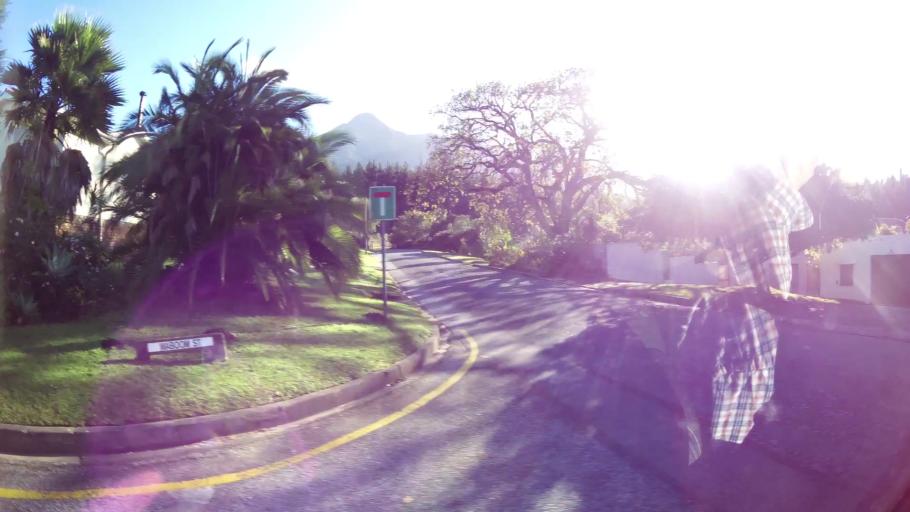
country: ZA
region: Western Cape
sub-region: Eden District Municipality
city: George
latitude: -33.9407
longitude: 22.4572
